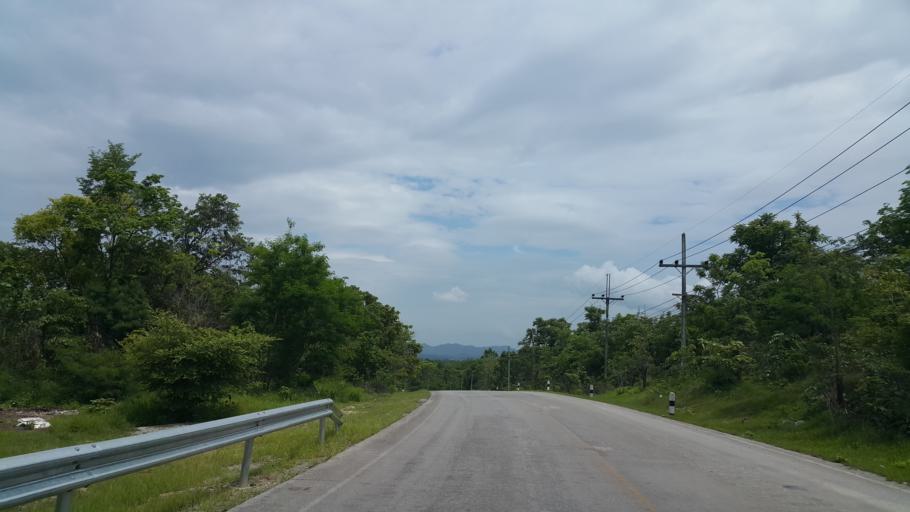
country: TH
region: Lampang
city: Mueang Pan
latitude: 18.7730
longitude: 99.5521
